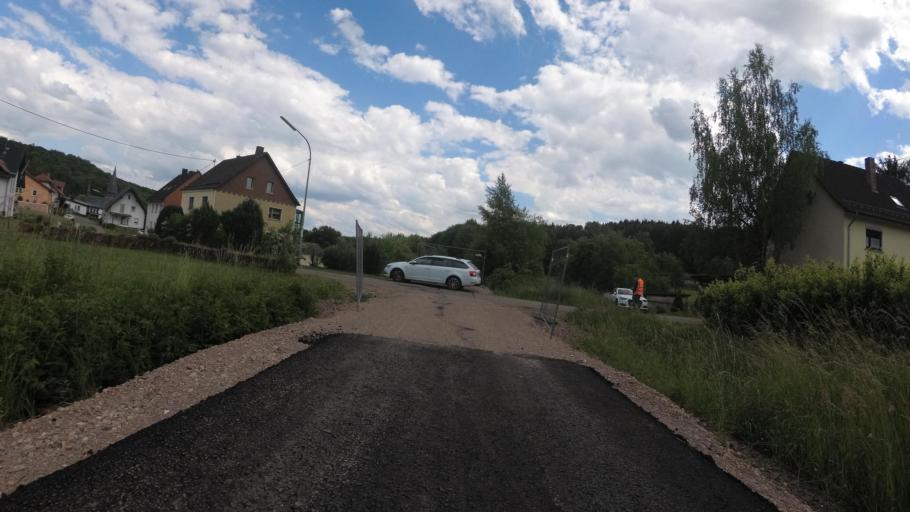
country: DE
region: Saarland
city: Nonnweiler
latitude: 49.6062
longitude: 6.9664
